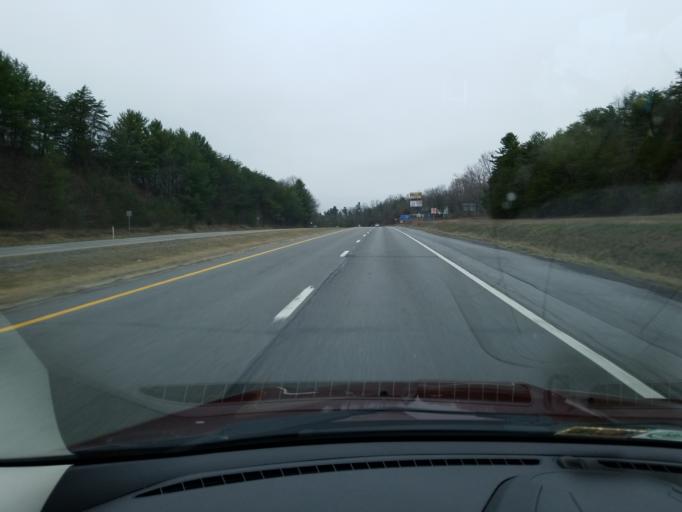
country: US
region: West Virginia
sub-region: Mercer County
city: Athens
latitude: 37.3618
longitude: -81.0294
